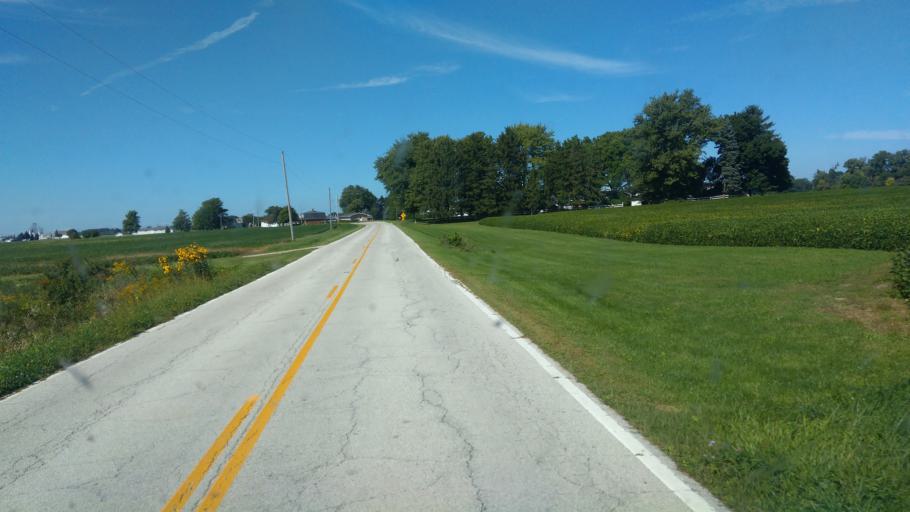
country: US
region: Ohio
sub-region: Ottawa County
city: Port Clinton
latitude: 41.4045
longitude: -82.8919
